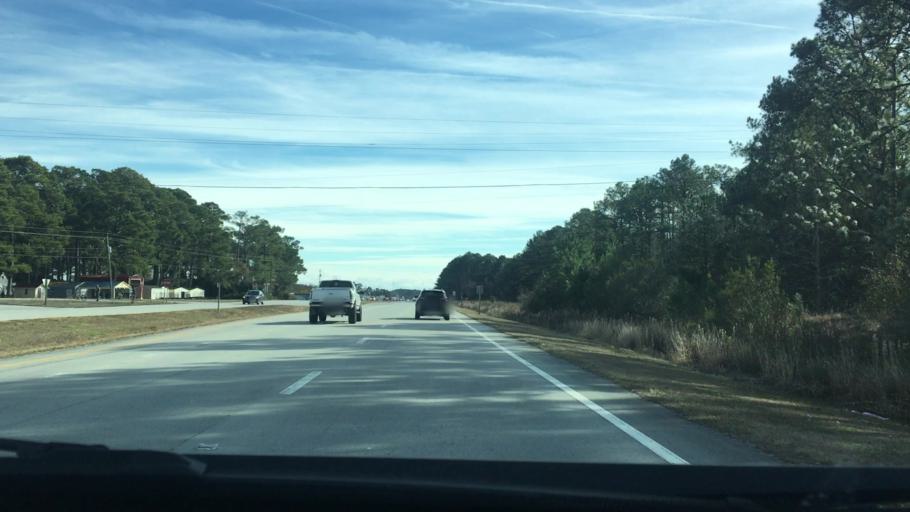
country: US
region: North Carolina
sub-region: Carteret County
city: Newport
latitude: 34.7611
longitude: -76.8536
